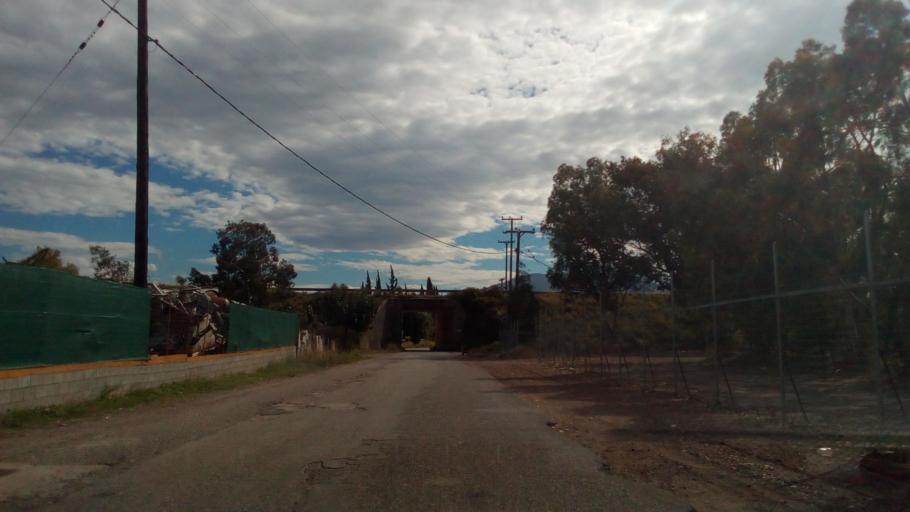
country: GR
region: West Greece
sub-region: Nomos Aitolias kai Akarnanias
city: Nafpaktos
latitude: 38.4097
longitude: 21.8832
